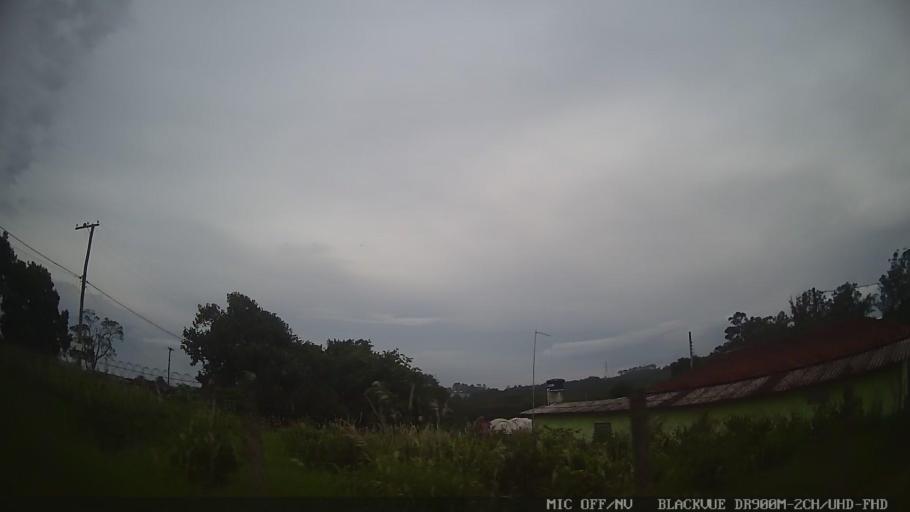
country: BR
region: Sao Paulo
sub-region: Suzano
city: Suzano
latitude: -23.6811
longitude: -46.2564
